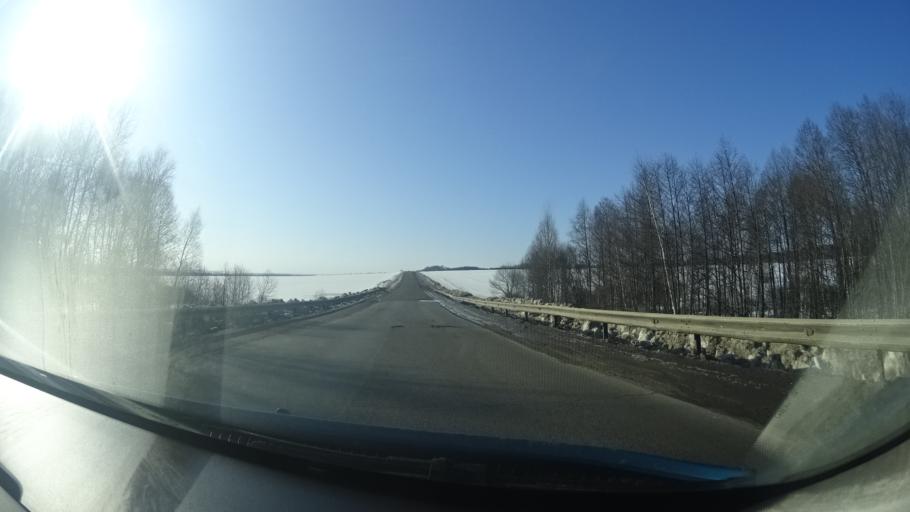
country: RU
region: Bashkortostan
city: Starobaltachevo
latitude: 56.0970
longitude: 55.9382
